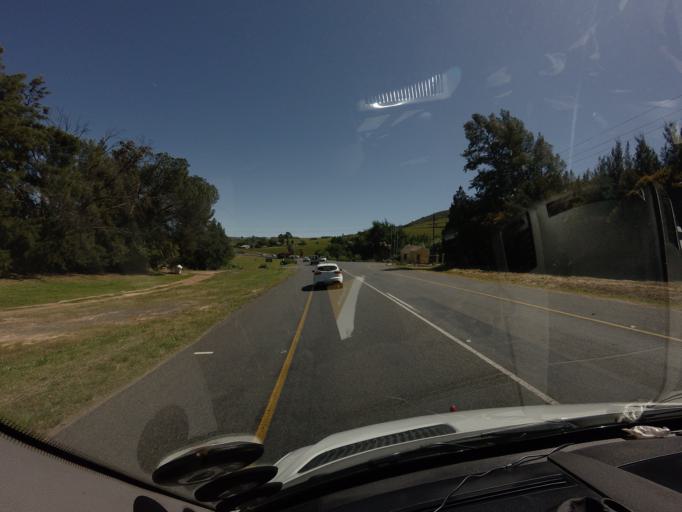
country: ZA
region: Western Cape
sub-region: Cape Winelands District Municipality
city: Stellenbosch
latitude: -33.8944
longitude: 18.8592
